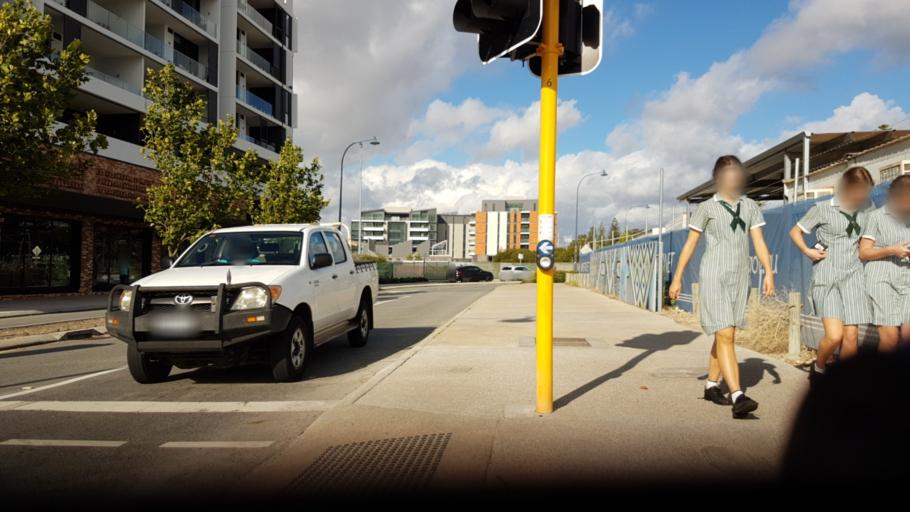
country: AU
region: Western Australia
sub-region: Claremont
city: Claremont
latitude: -31.9800
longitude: 115.7818
